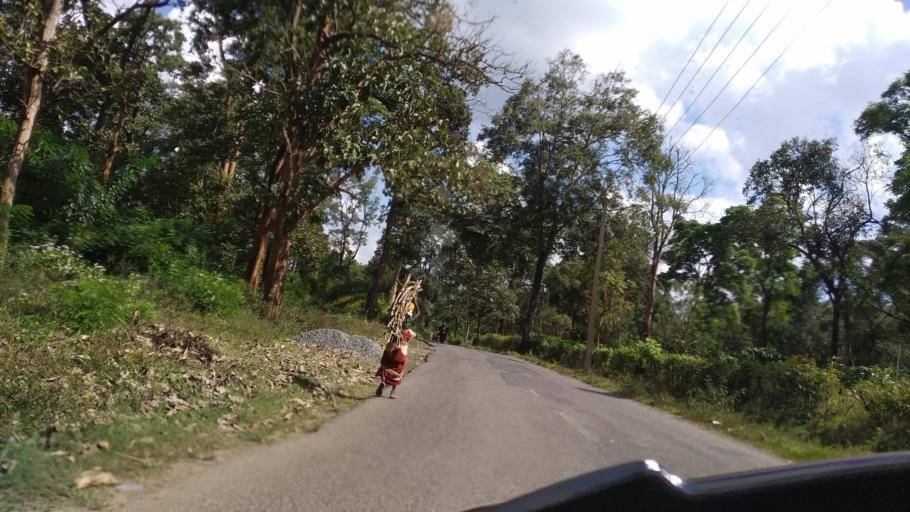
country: IN
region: Kerala
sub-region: Wayanad
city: Panamaram
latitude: 11.9536
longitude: 76.0640
